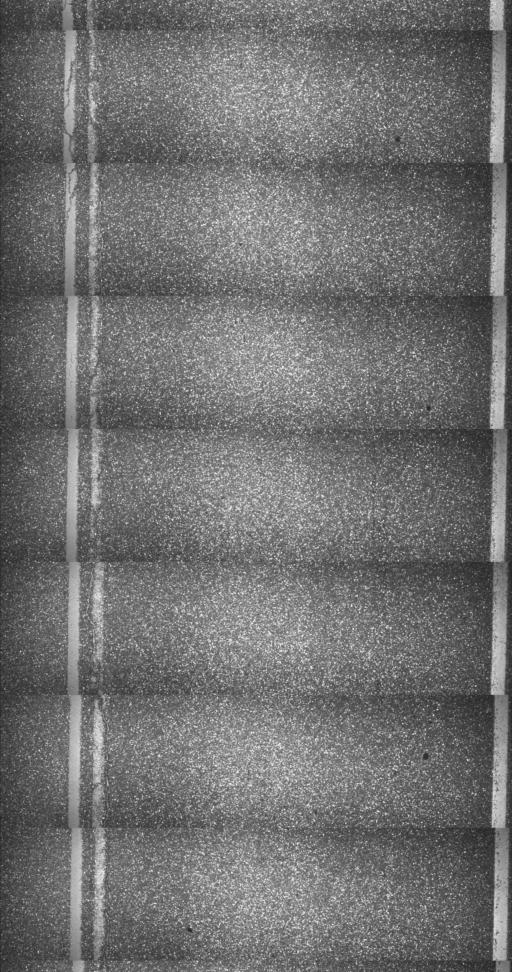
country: US
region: Vermont
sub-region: Washington County
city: Northfield
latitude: 44.1180
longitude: -72.7183
